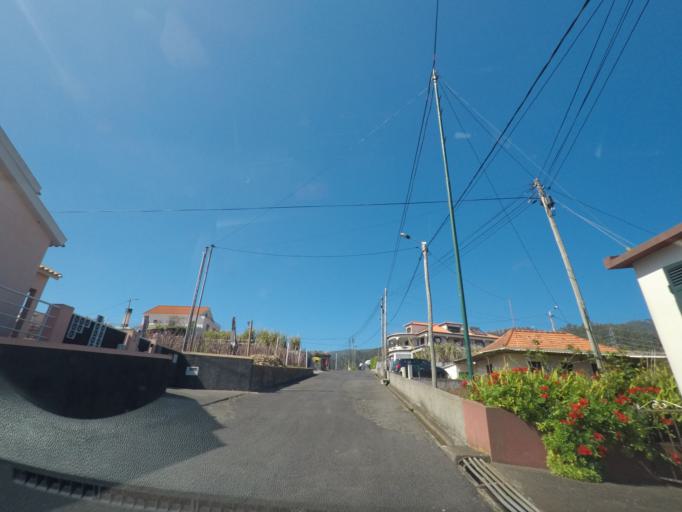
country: PT
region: Madeira
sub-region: Calheta
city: Arco da Calheta
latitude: 32.7045
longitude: -17.1163
